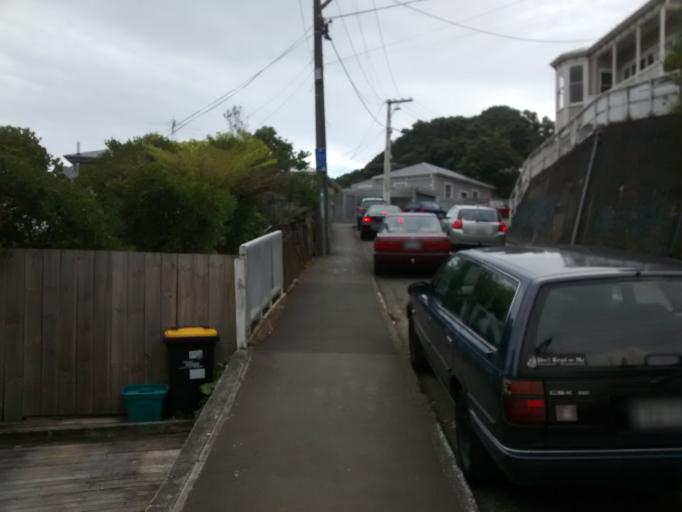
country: NZ
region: Wellington
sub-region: Wellington City
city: Wellington
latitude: -41.2971
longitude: 174.7690
